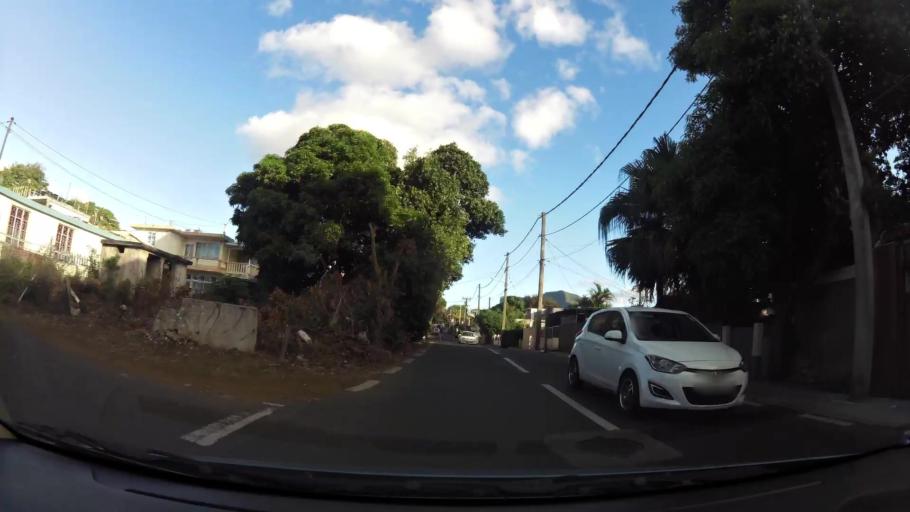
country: MU
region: Black River
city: Petite Riviere
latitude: -20.2220
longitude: 57.4636
